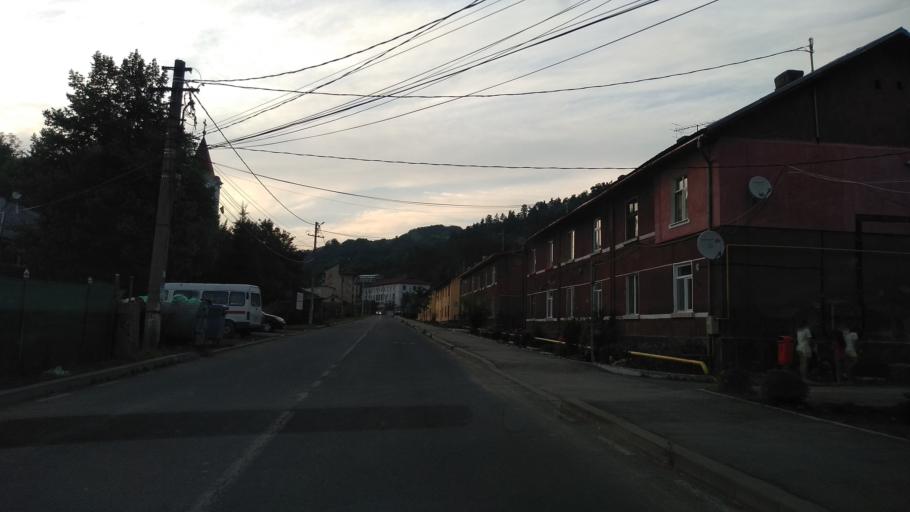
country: RO
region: Hunedoara
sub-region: Comuna Aninoasa
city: Aninoasa
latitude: 45.4044
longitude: 23.3207
